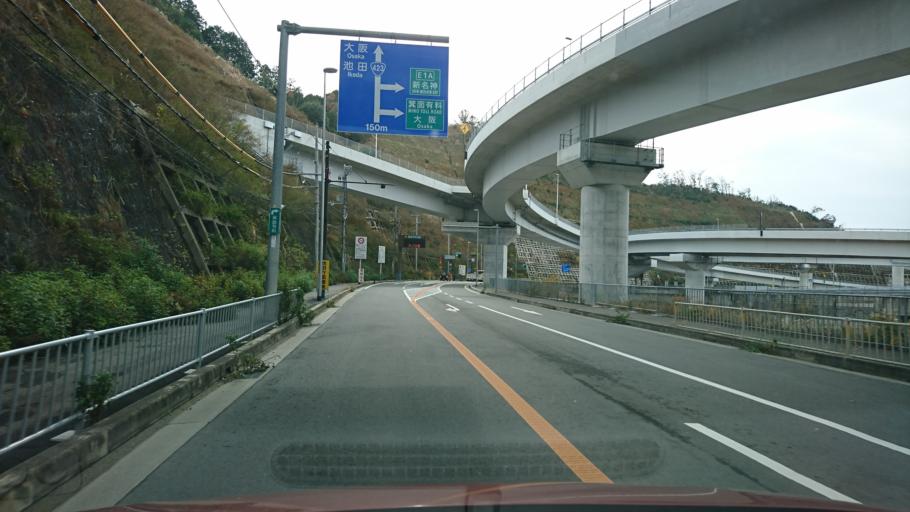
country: JP
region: Osaka
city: Mino
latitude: 34.8764
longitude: 135.4560
